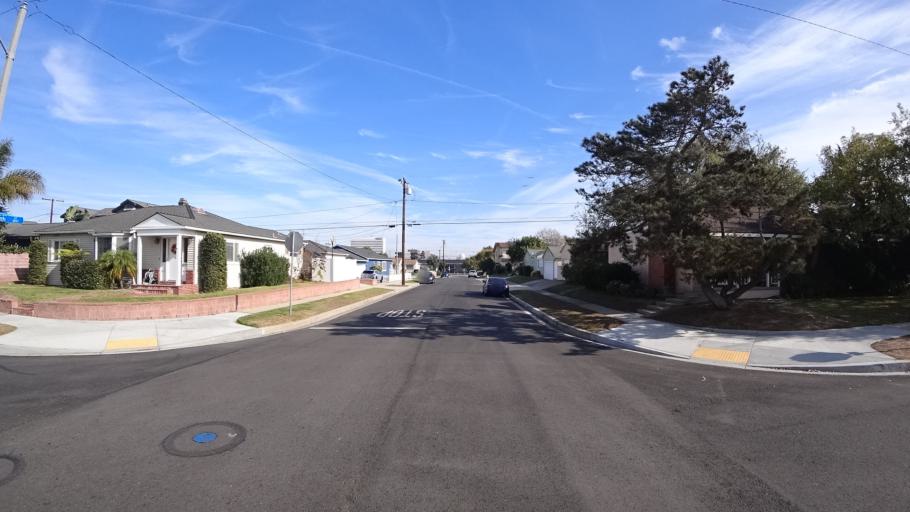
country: US
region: California
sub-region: Los Angeles County
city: Del Aire
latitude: 33.8919
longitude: -118.3809
